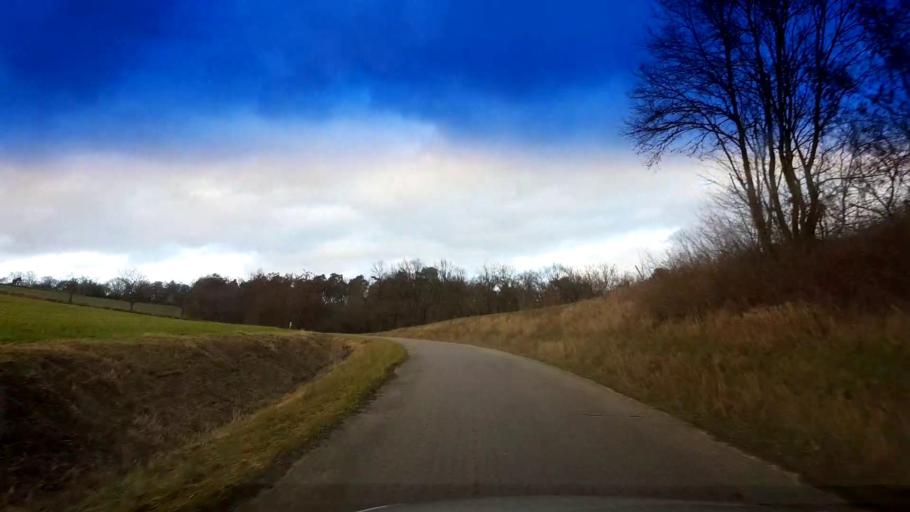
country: DE
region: Bavaria
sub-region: Regierungsbezirk Unterfranken
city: Stettfeld
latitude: 49.9703
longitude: 10.7390
